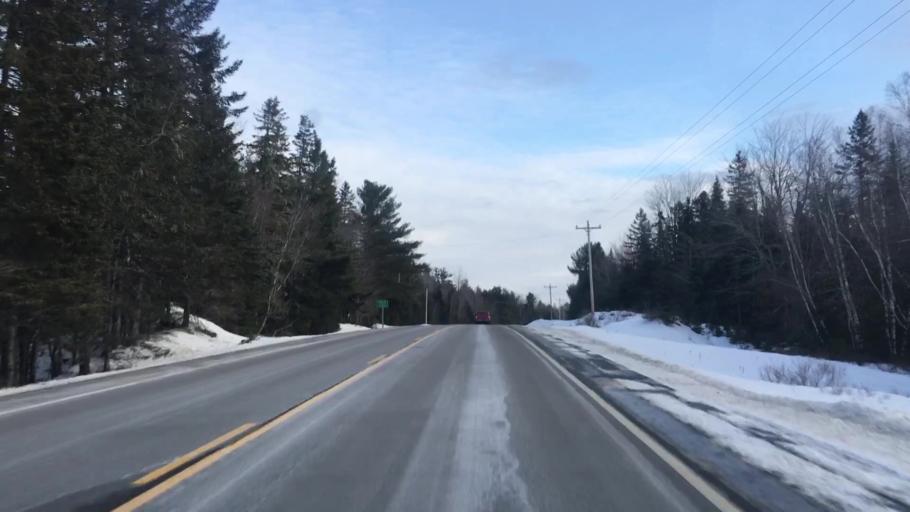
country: US
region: Maine
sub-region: Washington County
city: Machias
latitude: 44.9973
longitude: -67.6253
